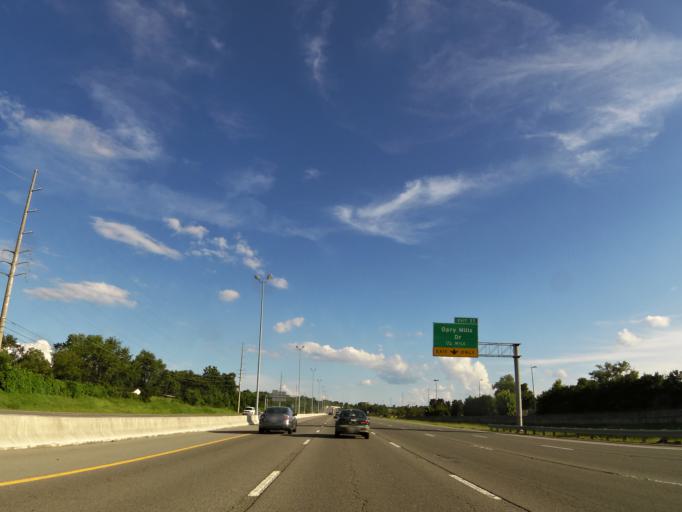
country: US
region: Tennessee
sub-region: Davidson County
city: Lakewood
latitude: 36.2074
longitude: -86.6905
